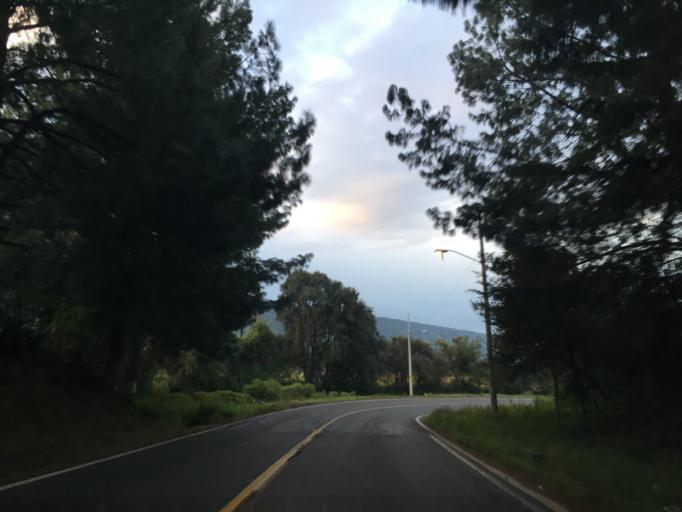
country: MX
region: Michoacan
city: Cheran
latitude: 19.6895
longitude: -101.9632
